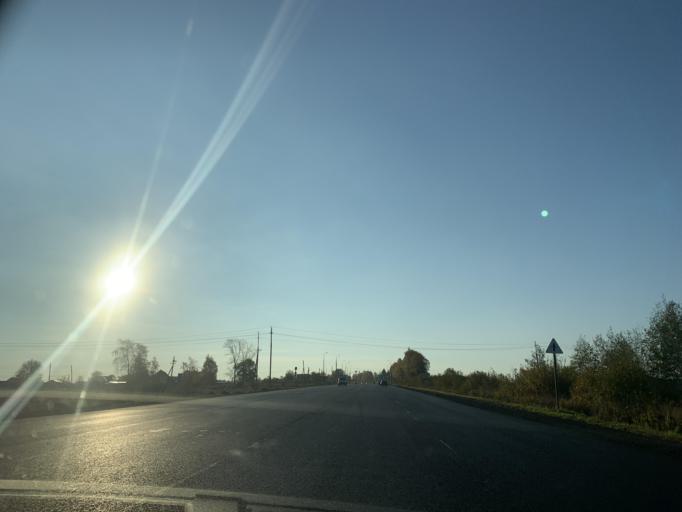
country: RU
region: Jaroslavl
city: Konstantinovskiy
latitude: 57.7919
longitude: 39.6060
